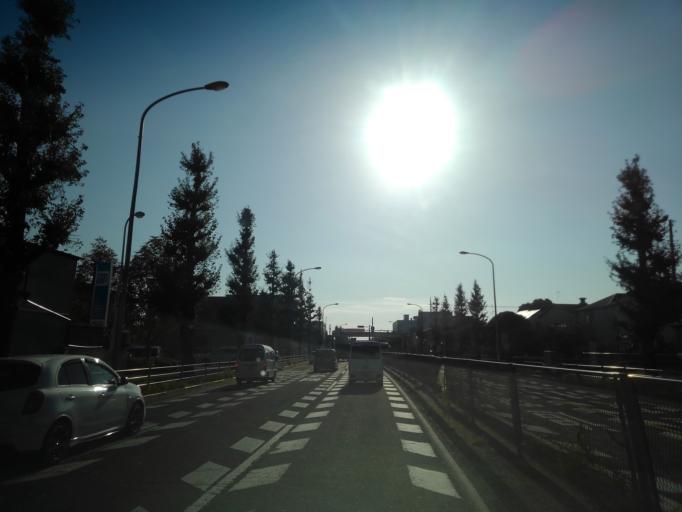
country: JP
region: Tokyo
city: Fussa
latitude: 35.7093
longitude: 139.3428
